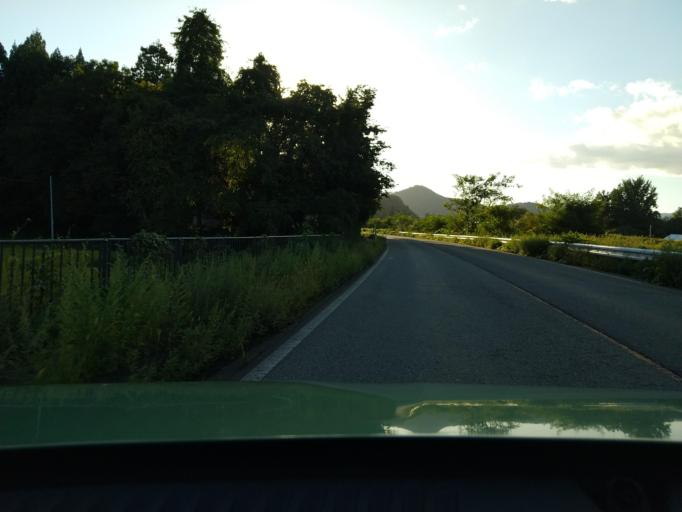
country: JP
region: Akita
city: Kakunodatemachi
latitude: 39.6099
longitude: 140.5730
